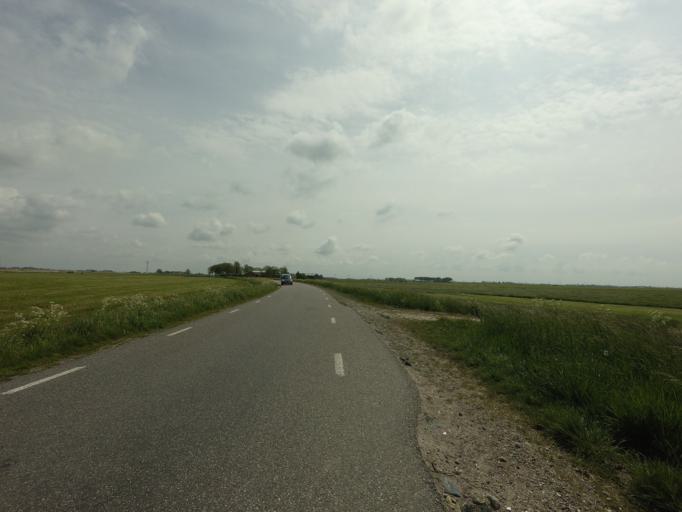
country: NL
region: Friesland
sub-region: Sudwest Fryslan
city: Bolsward
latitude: 53.1087
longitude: 5.4923
